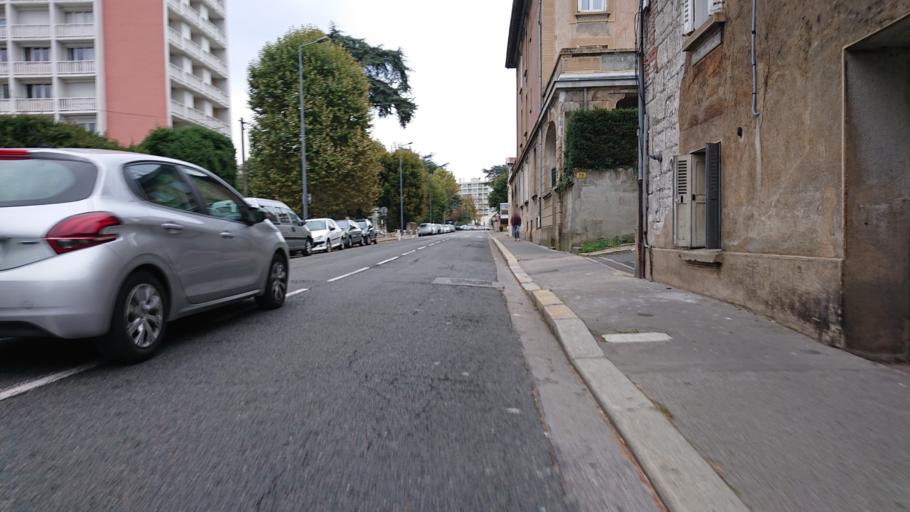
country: FR
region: Rhone-Alpes
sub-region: Departement de la Loire
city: Saint-Etienne
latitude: 45.4368
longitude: 4.4093
